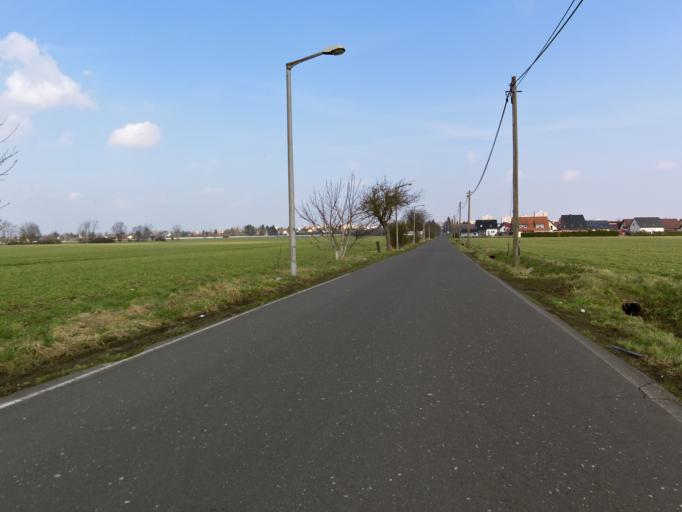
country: DE
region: Saxony
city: Markranstadt
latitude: 51.3034
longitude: 12.2934
